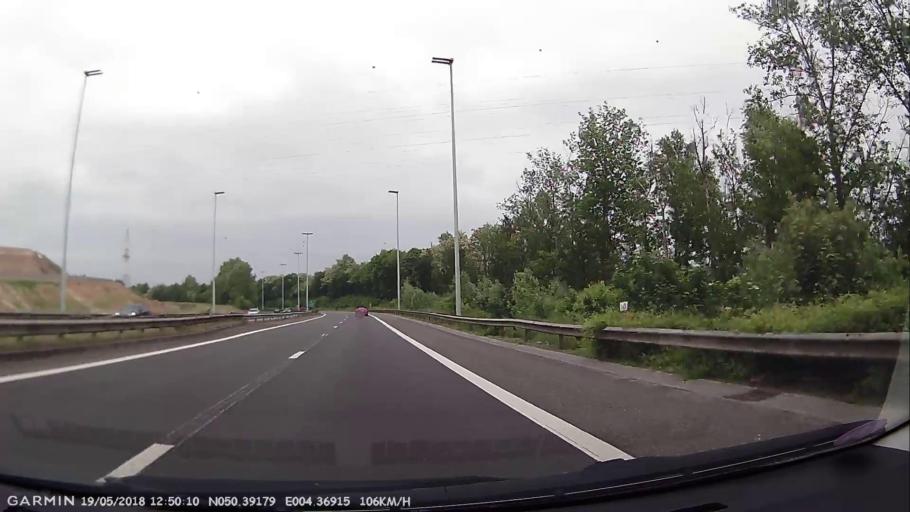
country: BE
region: Wallonia
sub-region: Province du Hainaut
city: Courcelles
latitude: 50.3922
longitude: 4.3691
